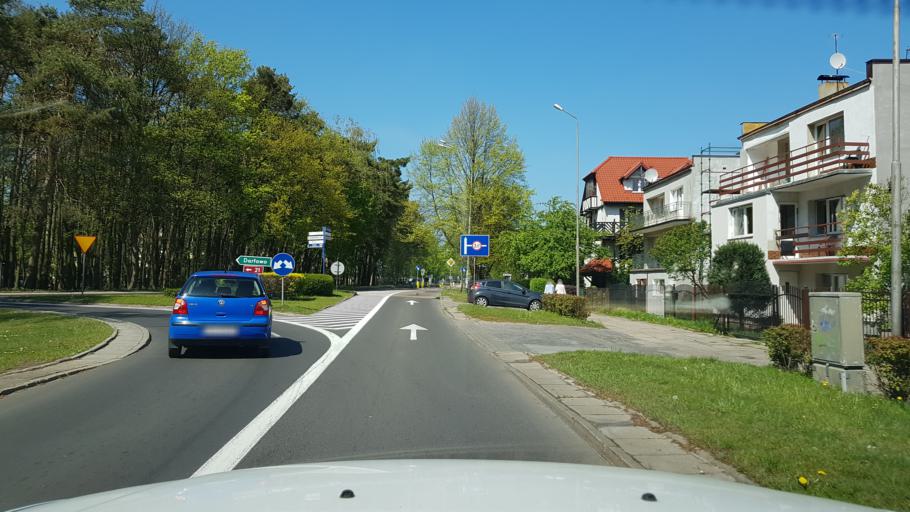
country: PL
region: Pomeranian Voivodeship
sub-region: Powiat slupski
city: Ustka
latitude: 54.5763
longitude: 16.8676
